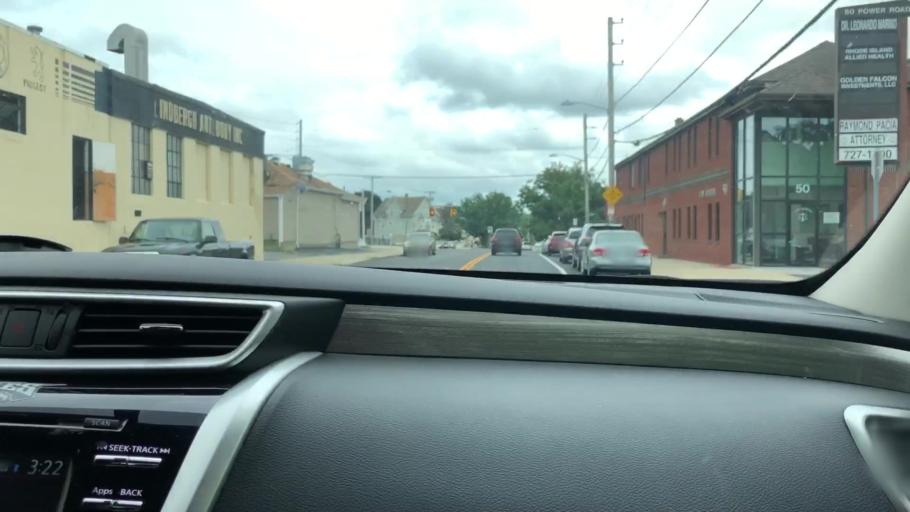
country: US
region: Rhode Island
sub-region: Providence County
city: Pawtucket
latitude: 41.8608
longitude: -71.4120
